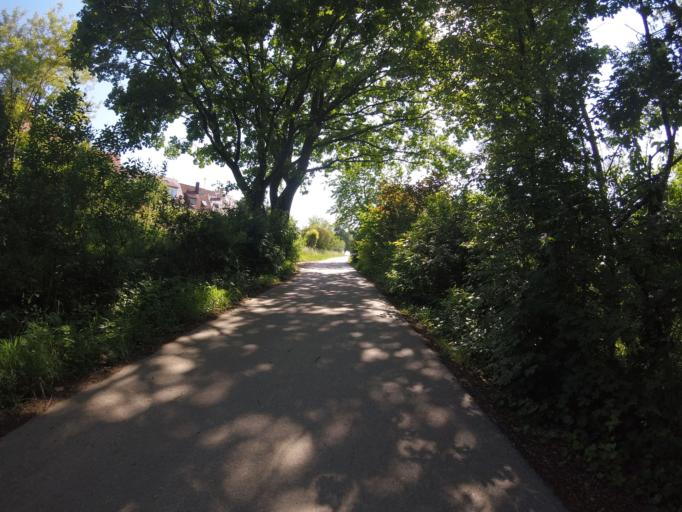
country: DE
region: Baden-Wuerttemberg
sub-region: Regierungsbezirk Stuttgart
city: Grossbottwar
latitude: 48.9736
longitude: 9.3173
